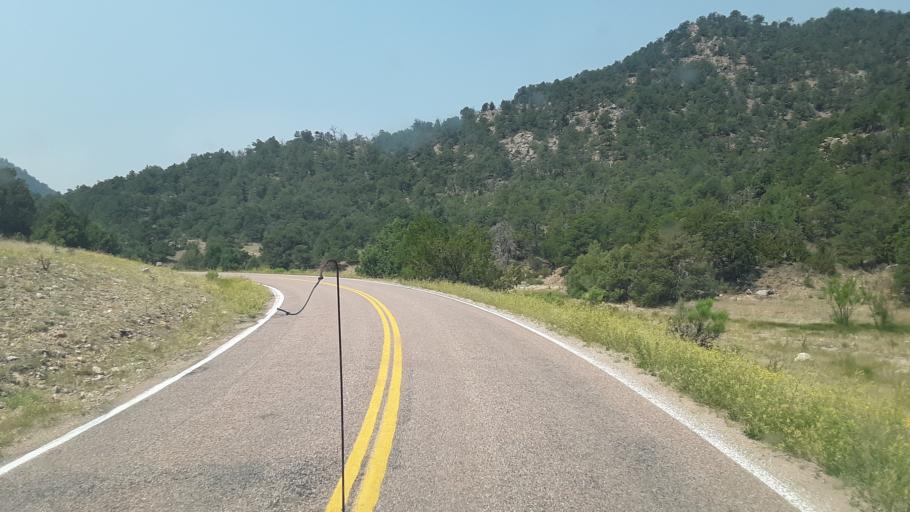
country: US
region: Colorado
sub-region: Fremont County
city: Canon City
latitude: 38.4278
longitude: -105.4020
